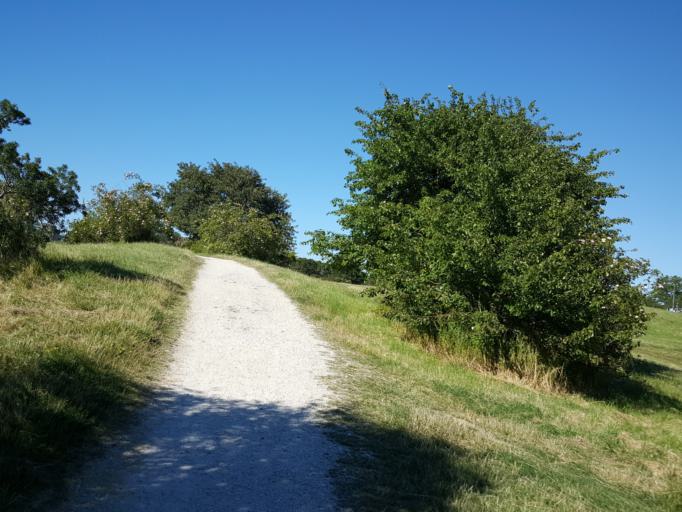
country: SE
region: Gotland
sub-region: Gotland
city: Visby
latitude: 57.6409
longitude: 18.3010
